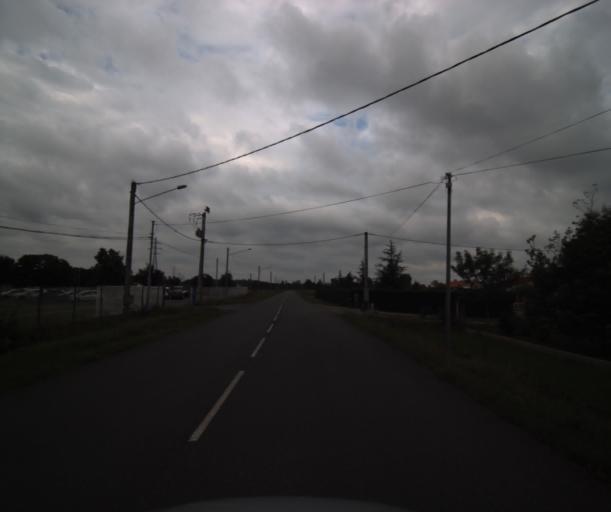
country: FR
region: Midi-Pyrenees
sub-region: Departement de la Haute-Garonne
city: Seysses
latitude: 43.4588
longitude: 1.3074
